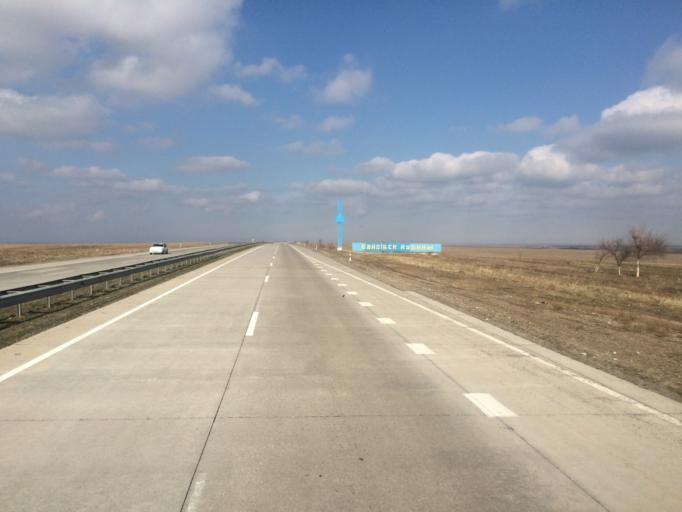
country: KZ
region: Ongtustik Qazaqstan
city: Temirlanovka
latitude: 42.7140
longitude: 69.2079
